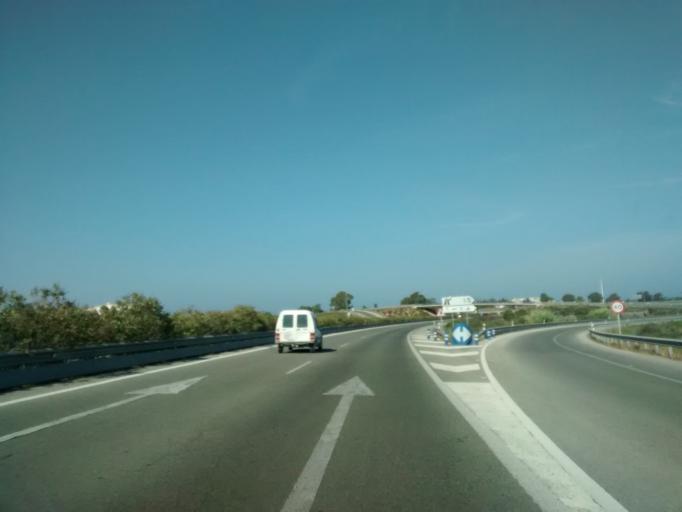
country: ES
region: Andalusia
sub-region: Provincia de Cadiz
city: Conil de la Frontera
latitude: 36.3555
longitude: -6.0997
